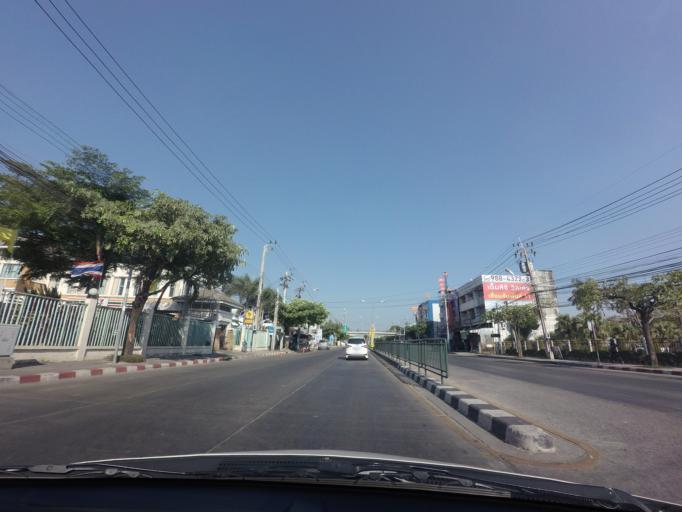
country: TH
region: Bangkok
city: Nong Chok
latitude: 13.8558
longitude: 100.8590
